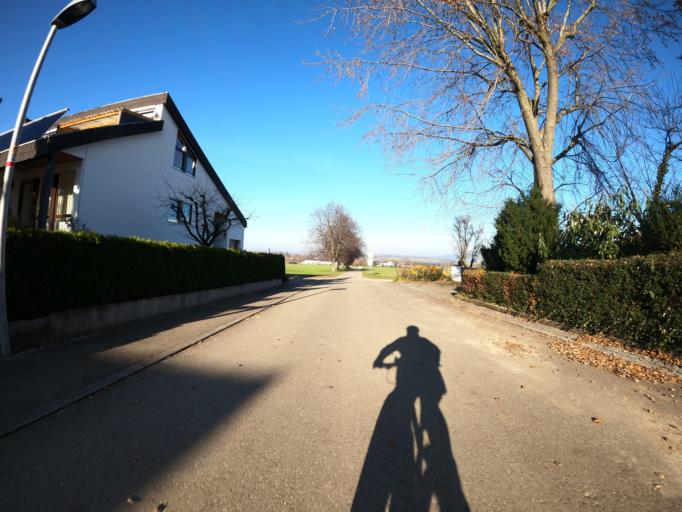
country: DE
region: Baden-Wuerttemberg
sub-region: Regierungsbezirk Stuttgart
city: Gammelshausen
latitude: 48.6450
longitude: 9.6526
